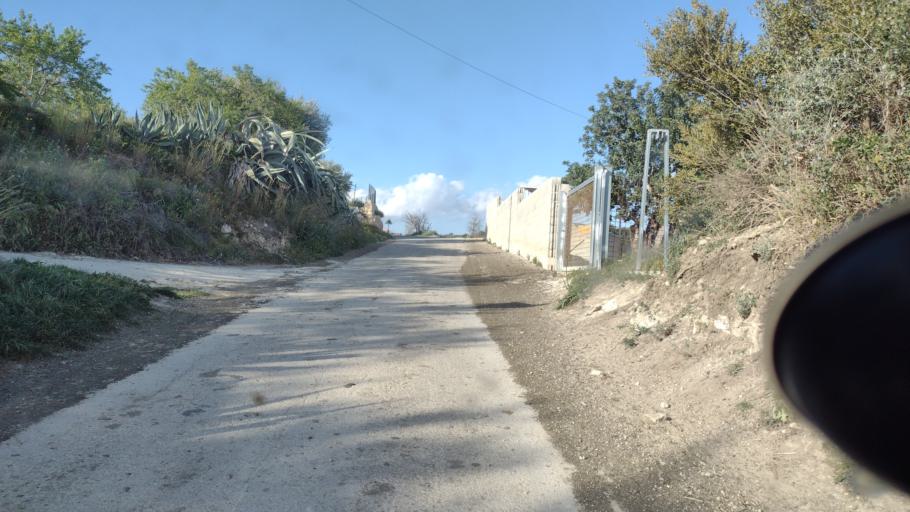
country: IT
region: Sicily
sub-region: Provincia di Siracusa
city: Noto
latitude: 36.8573
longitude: 15.0239
